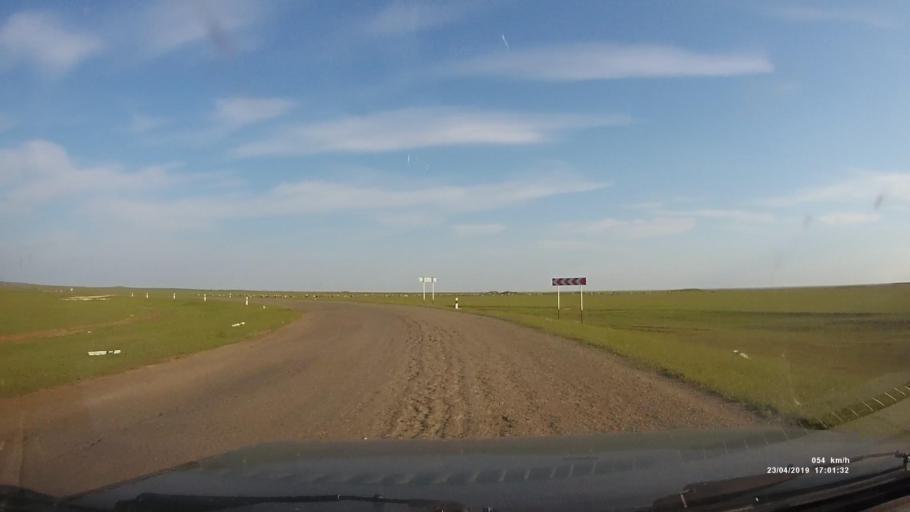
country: RU
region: Kalmykiya
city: Priyutnoye
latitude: 46.2953
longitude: 43.4082
